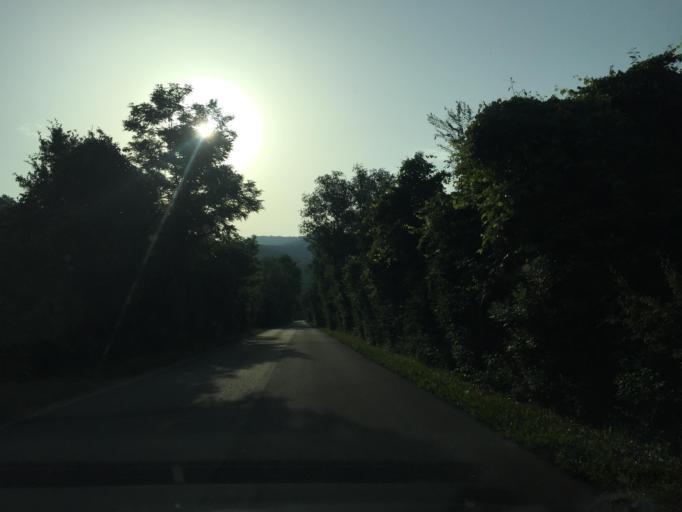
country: IT
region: Friuli Venezia Giulia
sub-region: Provincia di Trieste
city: Domio
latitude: 45.5881
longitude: 13.8236
